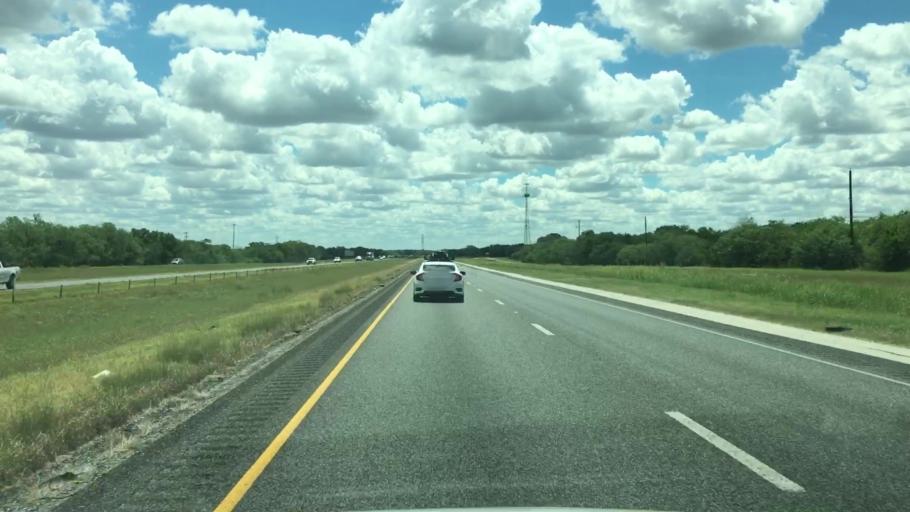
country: US
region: Texas
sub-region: Bexar County
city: Elmendorf
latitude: 29.2652
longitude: -98.3958
